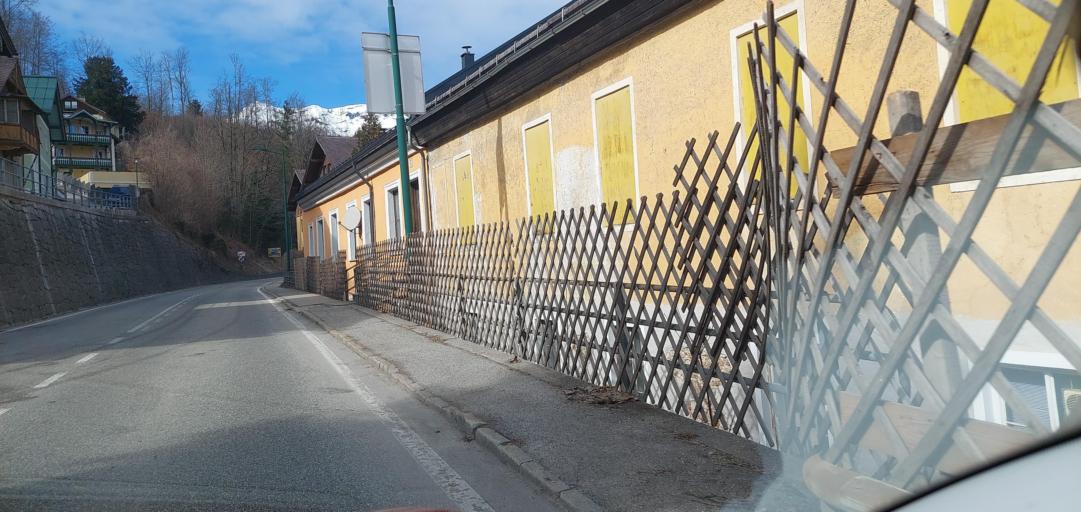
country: AT
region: Upper Austria
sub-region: Politischer Bezirk Gmunden
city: Bad Ischl
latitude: 47.7145
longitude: 13.6157
